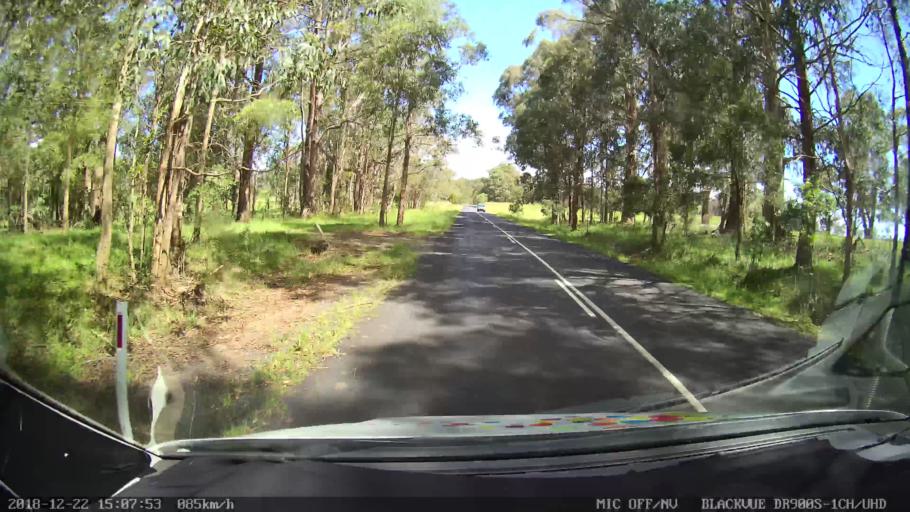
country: AU
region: New South Wales
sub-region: Bellingen
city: Dorrigo
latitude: -30.3050
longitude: 152.4126
